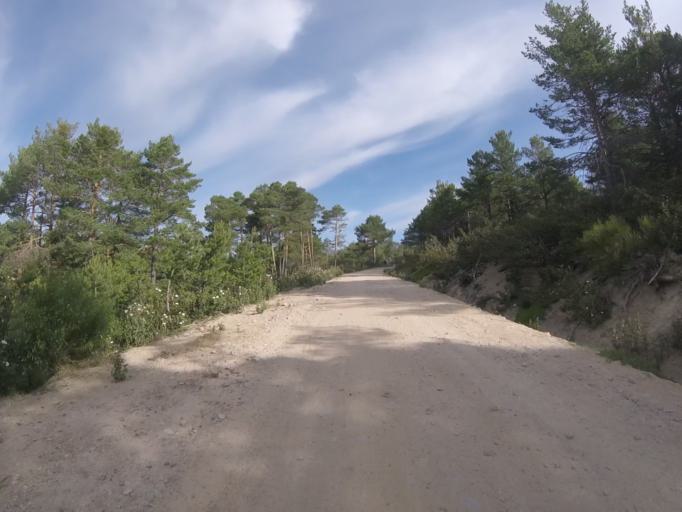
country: ES
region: Castille and Leon
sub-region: Provincia de Avila
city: Peguerinos
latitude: 40.6564
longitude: -4.1854
